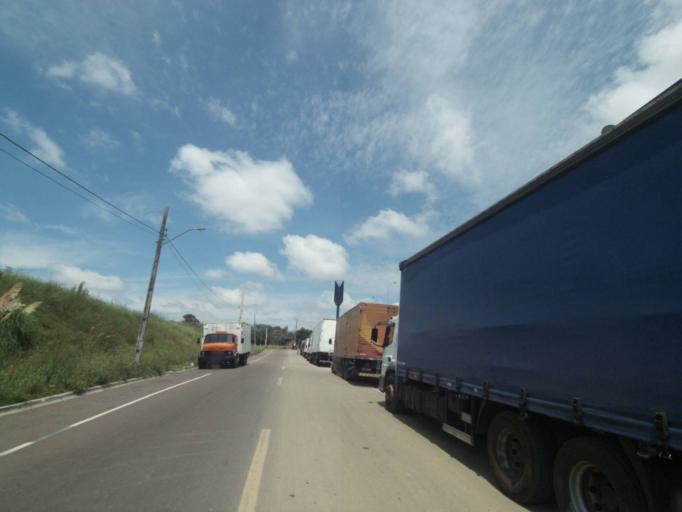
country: BR
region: Parana
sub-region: Curitiba
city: Curitiba
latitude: -25.4563
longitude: -49.3586
